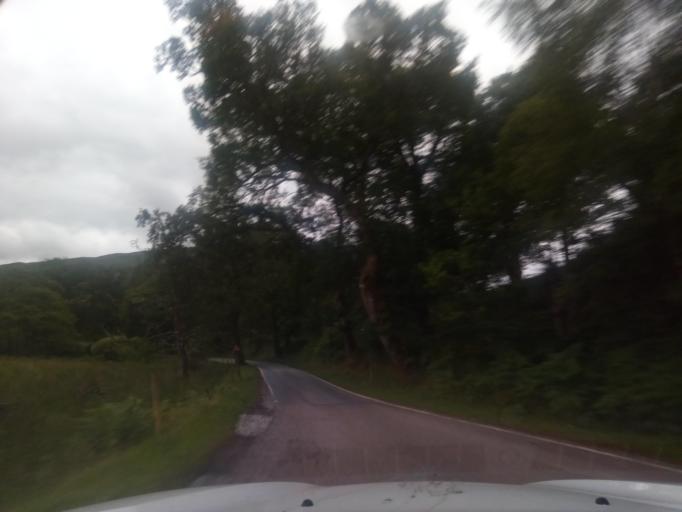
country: GB
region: Scotland
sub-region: Highland
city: Fort William
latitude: 56.8588
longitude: -5.3503
